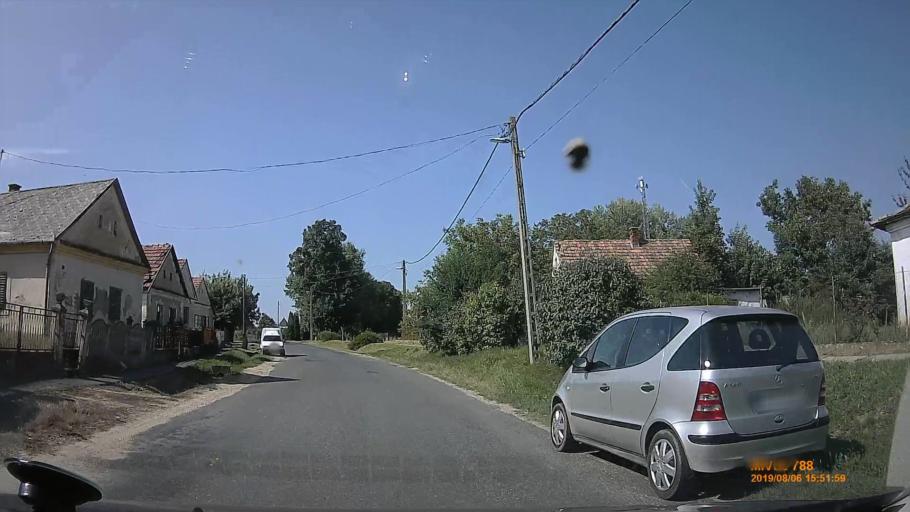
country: HU
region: Somogy
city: Csurgo
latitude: 46.2811
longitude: 17.0415
